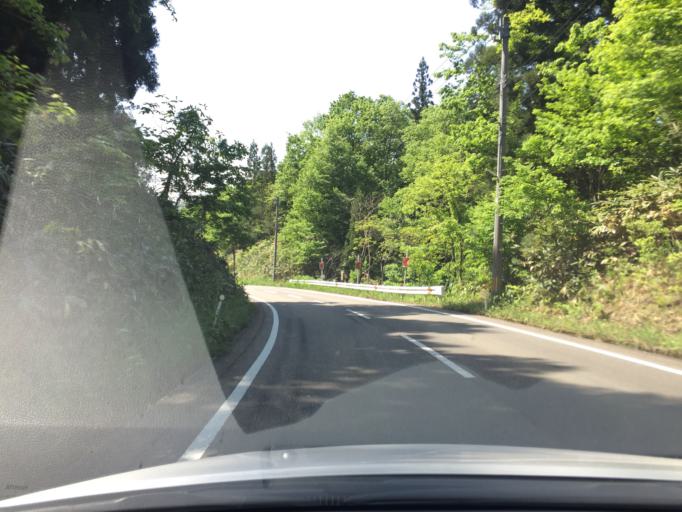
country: JP
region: Niigata
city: Kamo
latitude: 37.5585
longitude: 139.0777
